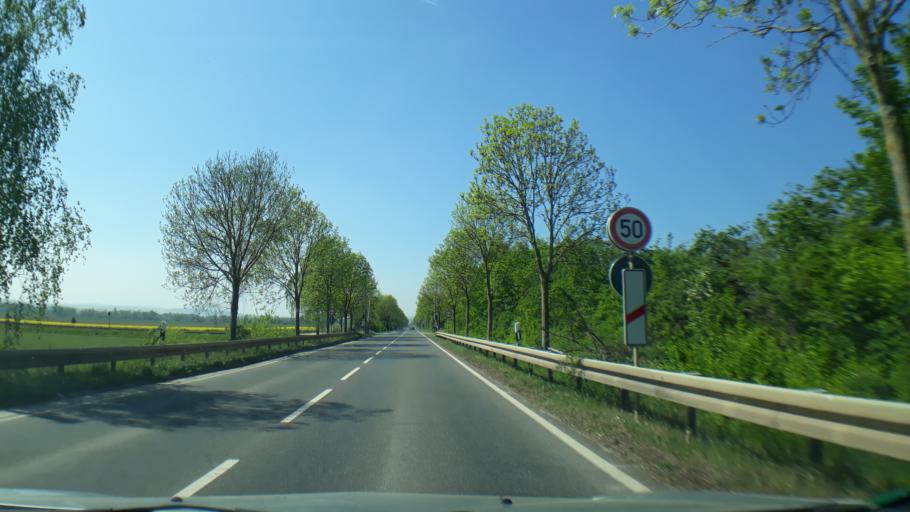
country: DE
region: North Rhine-Westphalia
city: Zulpich
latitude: 50.6923
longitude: 6.6754
